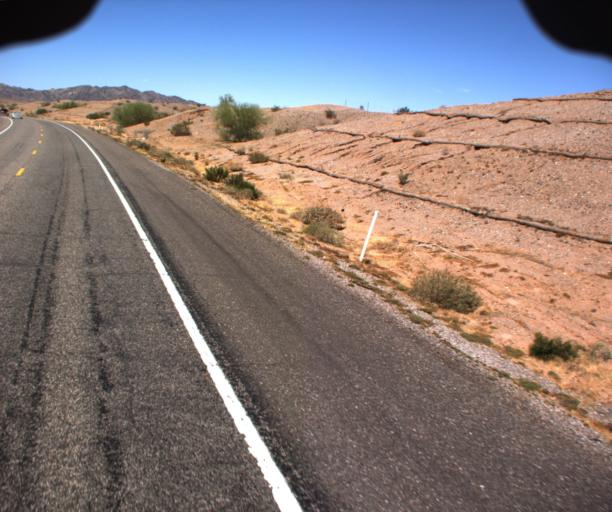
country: US
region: Arizona
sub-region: La Paz County
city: Parker
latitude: 33.9946
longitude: -114.1996
